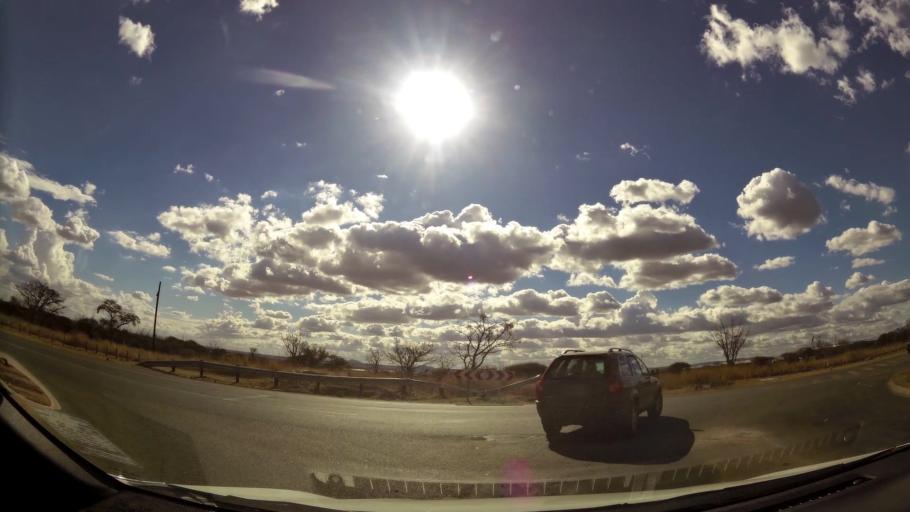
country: ZA
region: Limpopo
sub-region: Capricorn District Municipality
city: Polokwane
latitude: -23.8754
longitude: 29.4791
